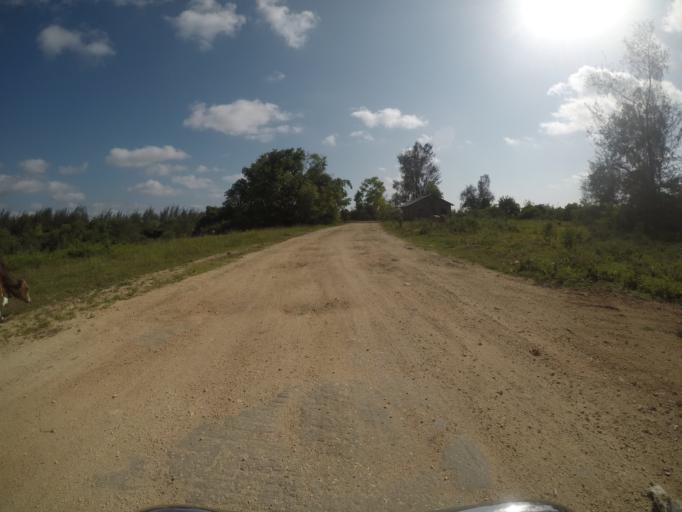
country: TZ
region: Zanzibar Central/South
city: Koani
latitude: -6.2171
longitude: 39.3327
